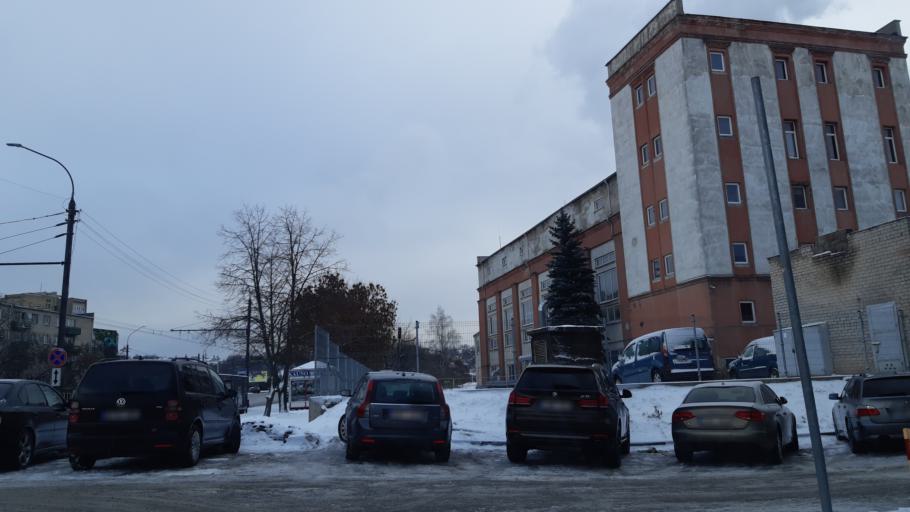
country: LT
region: Kauno apskritis
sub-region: Kaunas
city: Kaunas
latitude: 54.9144
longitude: 23.9026
